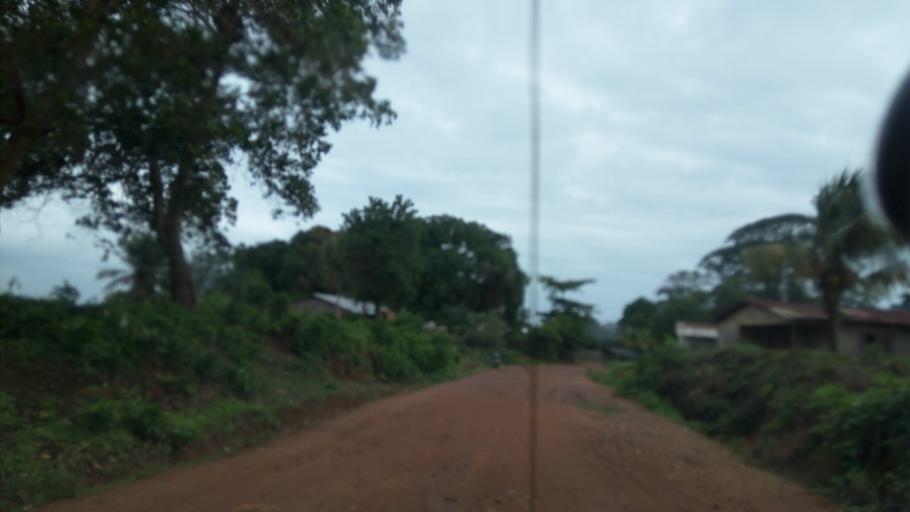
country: SL
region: Northern Province
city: Tintafor
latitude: 8.6304
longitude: -13.2191
